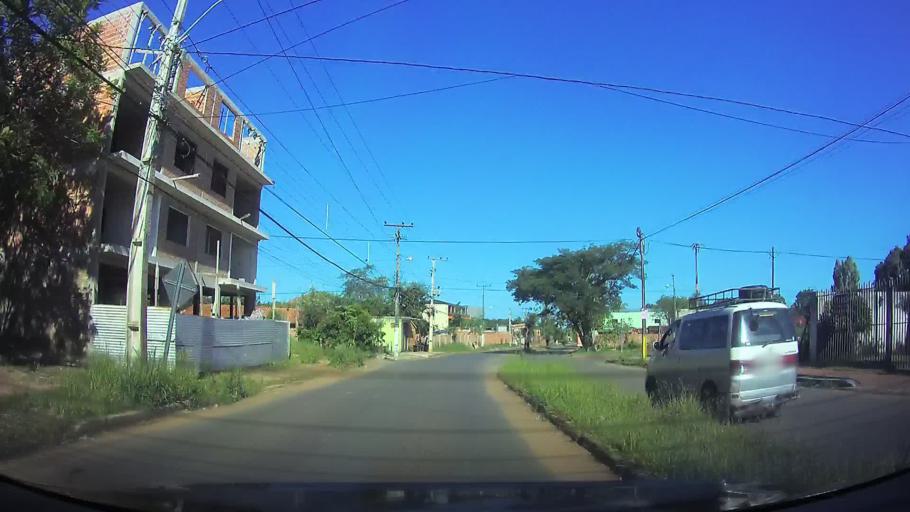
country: PY
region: Central
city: Fernando de la Mora
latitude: -25.2969
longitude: -57.5145
